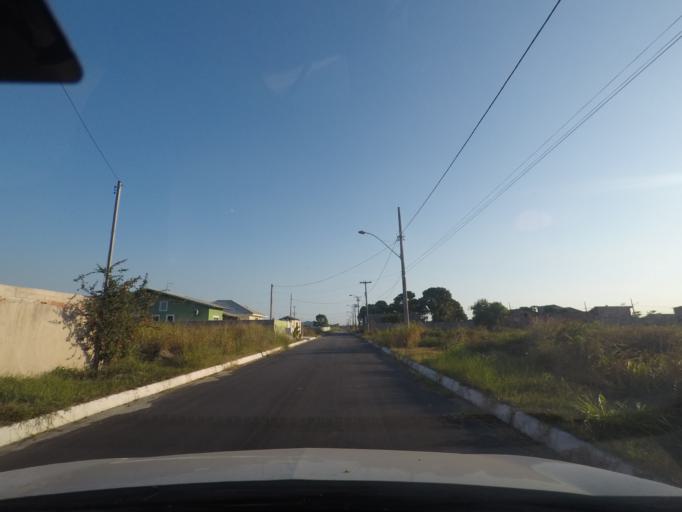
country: BR
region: Rio de Janeiro
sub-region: Marica
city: Marica
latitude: -22.9584
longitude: -42.9281
